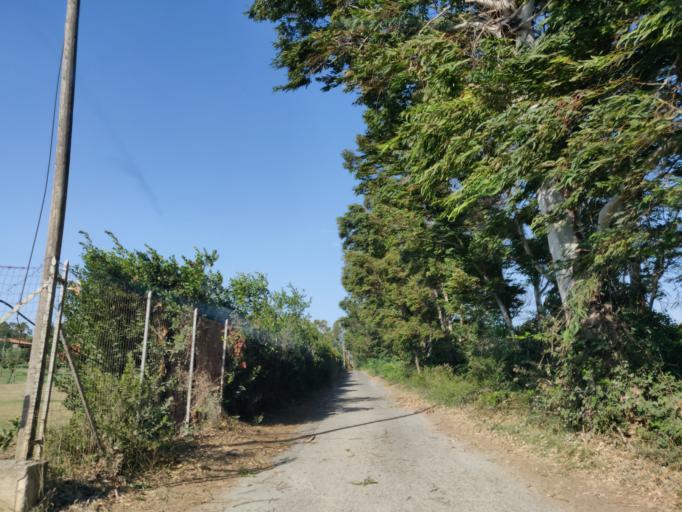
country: IT
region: Latium
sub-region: Citta metropolitana di Roma Capitale
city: Aurelia
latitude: 42.1374
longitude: 11.7612
